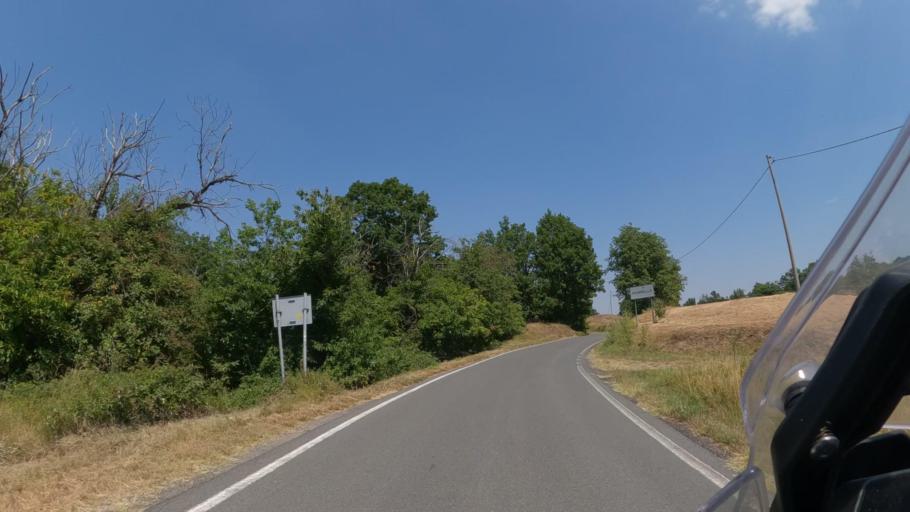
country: IT
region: Piedmont
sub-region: Provincia di Alessandria
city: Morbello
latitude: 44.5597
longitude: 8.5139
